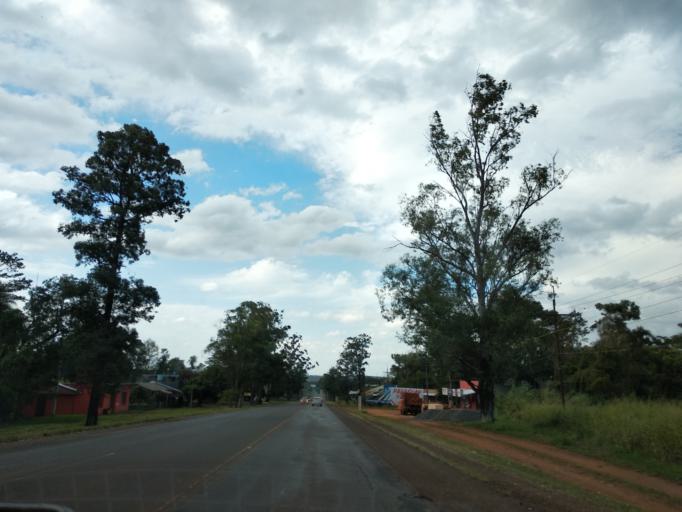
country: PY
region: Itapua
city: San Juan del Parana
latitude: -27.2931
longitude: -55.9288
